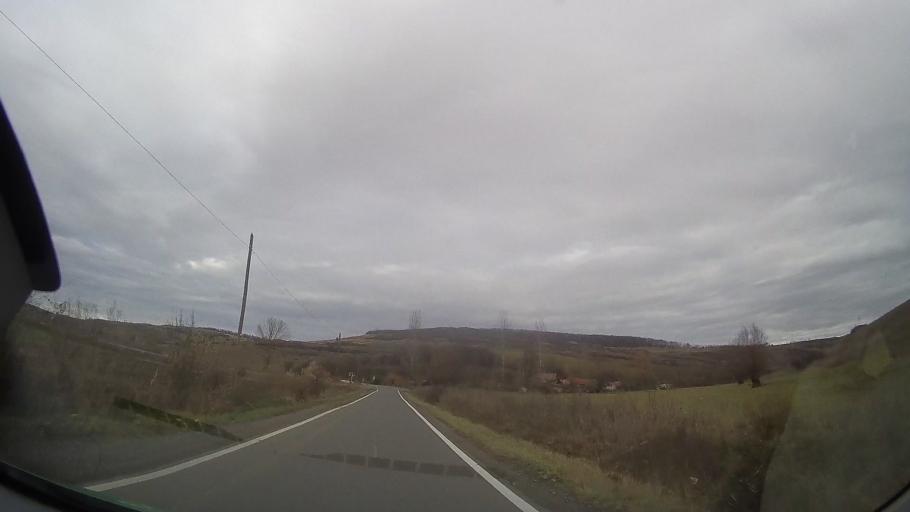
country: RO
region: Mures
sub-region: Comuna Cozma
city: Cozma
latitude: 46.7938
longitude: 24.5425
